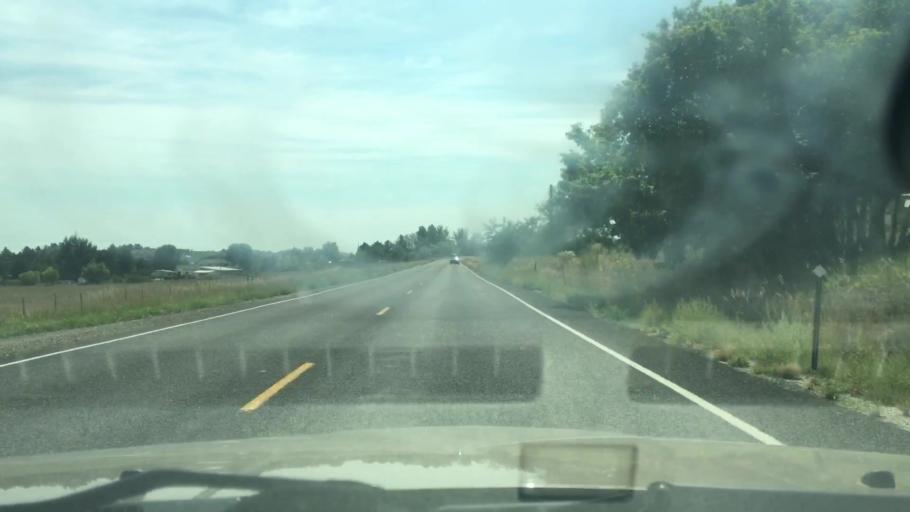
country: US
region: Colorado
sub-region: Larimer County
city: Loveland
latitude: 40.4449
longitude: -105.1968
